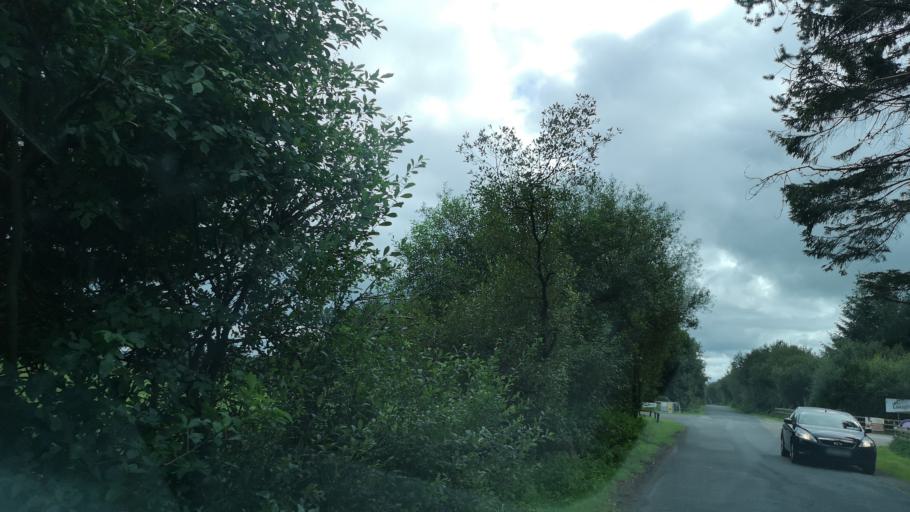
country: IE
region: Leinster
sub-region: Uibh Fhaili
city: Ferbane
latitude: 53.2254
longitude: -7.7283
